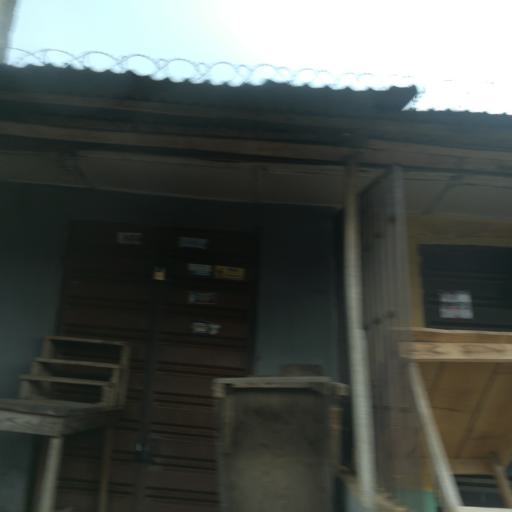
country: NG
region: Lagos
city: Agege
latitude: 6.5950
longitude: 3.2972
